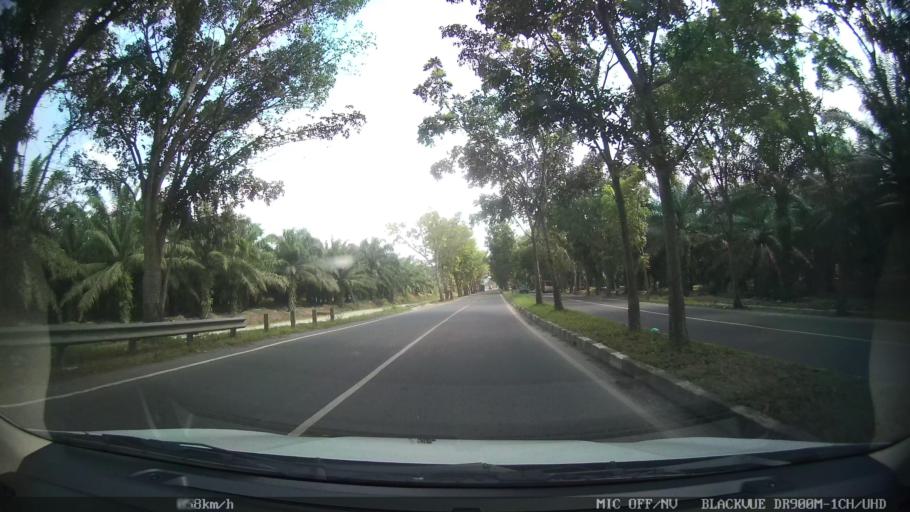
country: ID
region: North Sumatra
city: Binjai
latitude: 3.6503
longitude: 98.5355
